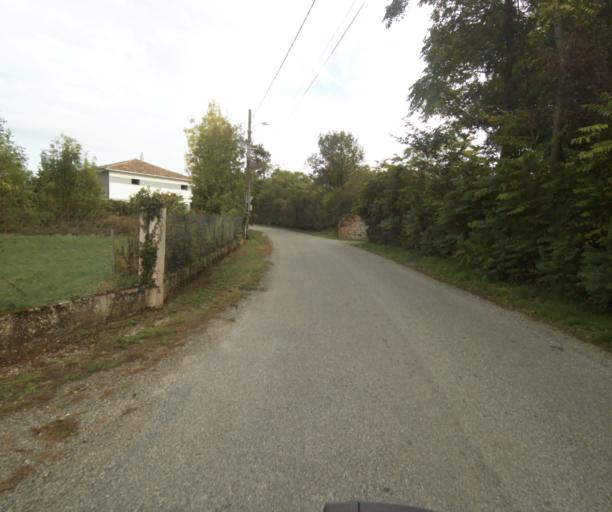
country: FR
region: Midi-Pyrenees
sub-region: Departement du Tarn-et-Garonne
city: Finhan
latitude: 43.9168
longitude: 1.2212
